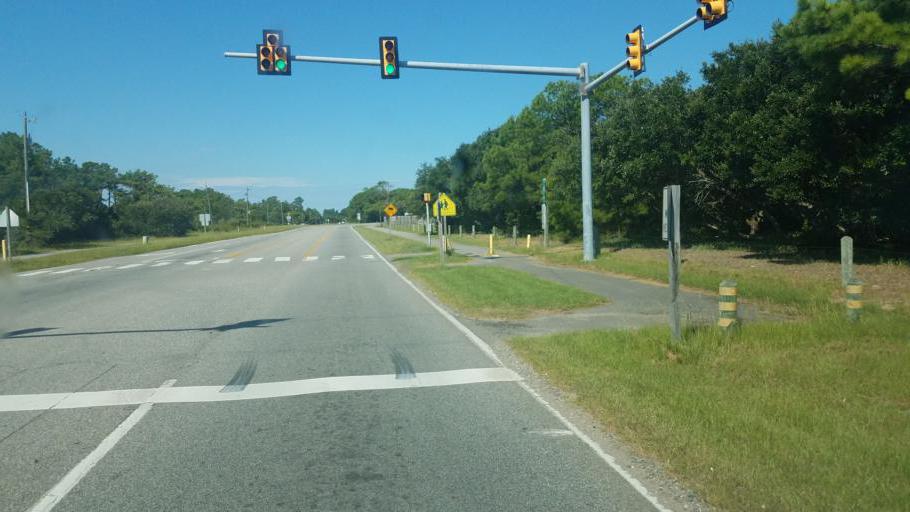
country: US
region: North Carolina
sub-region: Dare County
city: Kill Devil Hills
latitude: 36.0115
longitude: -75.6657
